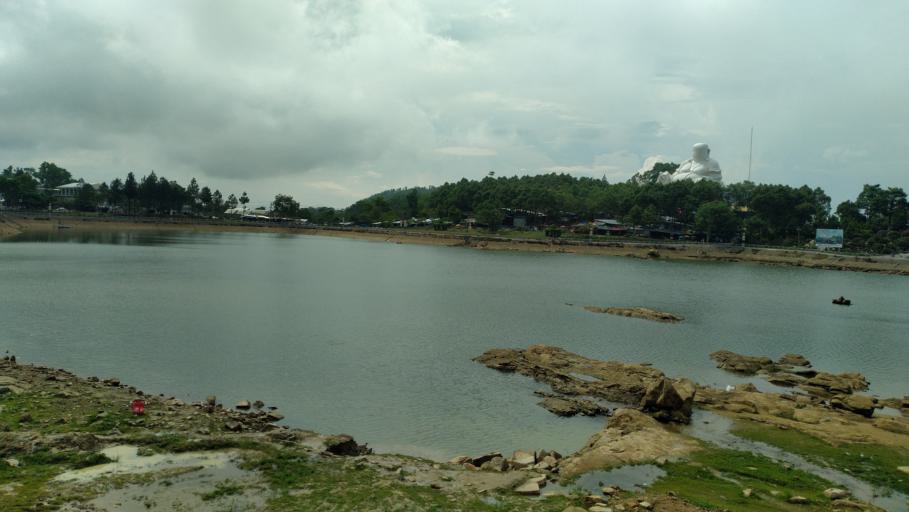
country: VN
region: An Giang
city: Tri Ton
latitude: 10.5030
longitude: 104.9843
